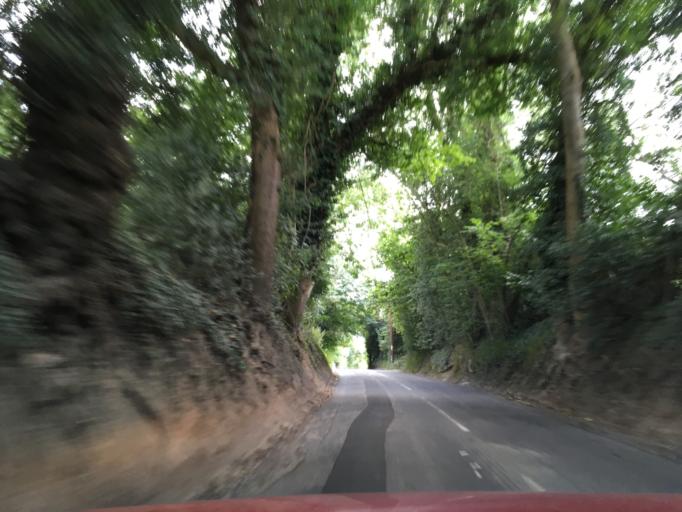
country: GB
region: England
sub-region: Kent
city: Yalding
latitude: 51.2416
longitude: 0.4503
